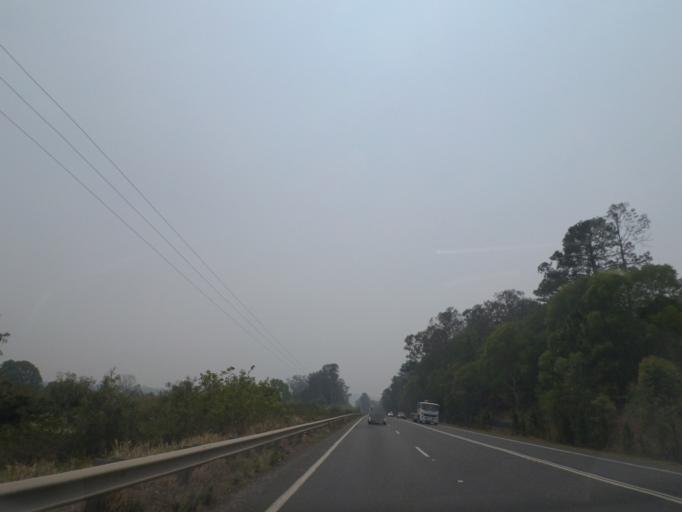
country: AU
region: New South Wales
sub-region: Clarence Valley
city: Maclean
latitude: -29.5583
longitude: 153.1504
